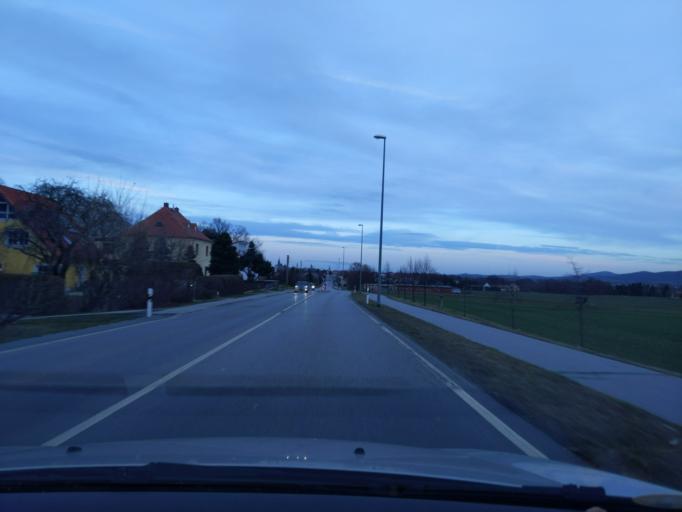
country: DE
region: Saxony
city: Obergurig
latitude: 51.1795
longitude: 14.3835
